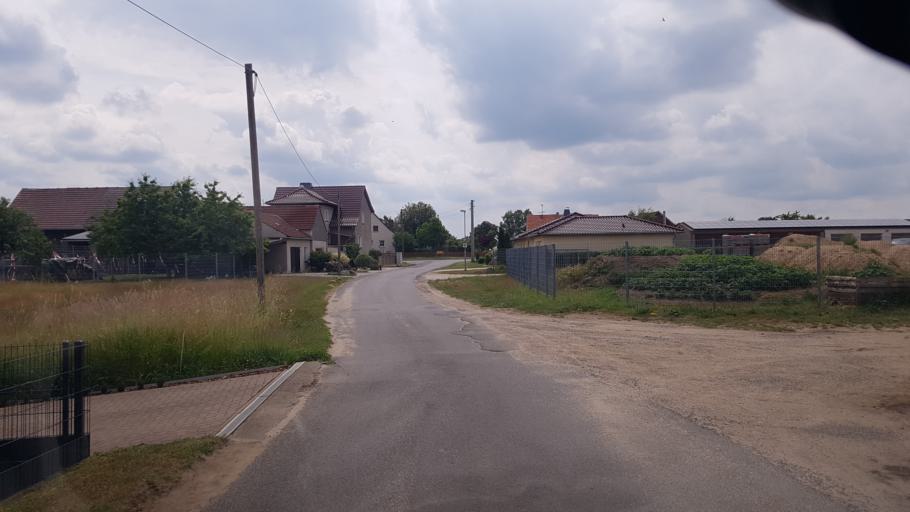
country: DE
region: Brandenburg
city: Lebusa
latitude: 51.8140
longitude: 13.4436
